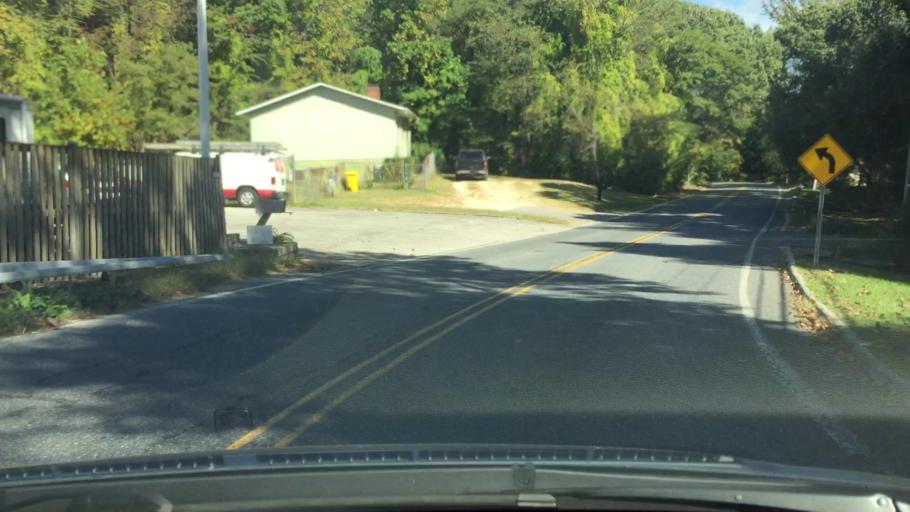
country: US
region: Maryland
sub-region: Anne Arundel County
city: Cape Saint Claire
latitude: 39.0527
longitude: -76.4678
